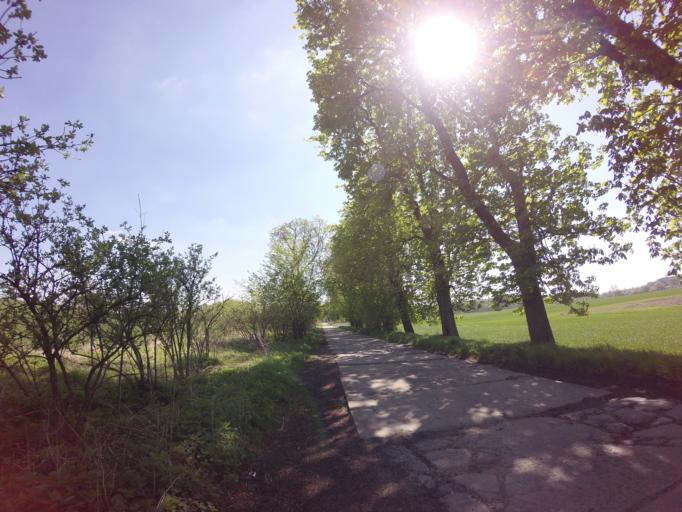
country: PL
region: West Pomeranian Voivodeship
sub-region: Powiat stargardzki
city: Suchan
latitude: 53.1856
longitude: 15.3191
